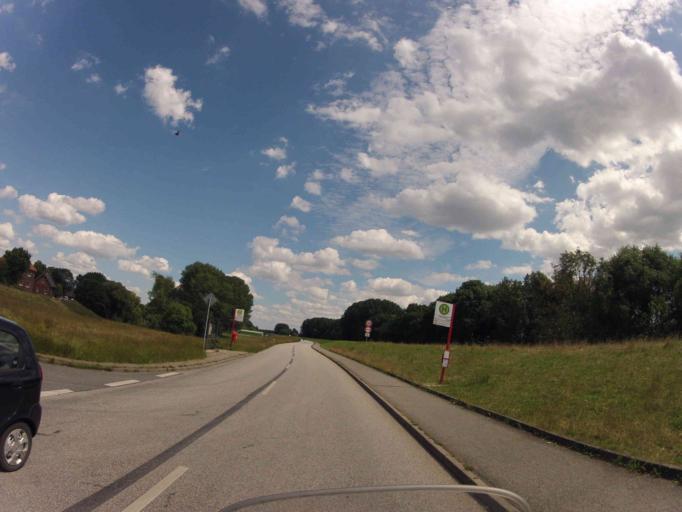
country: DE
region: Lower Saxony
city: Stelle
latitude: 53.4006
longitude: 10.1682
